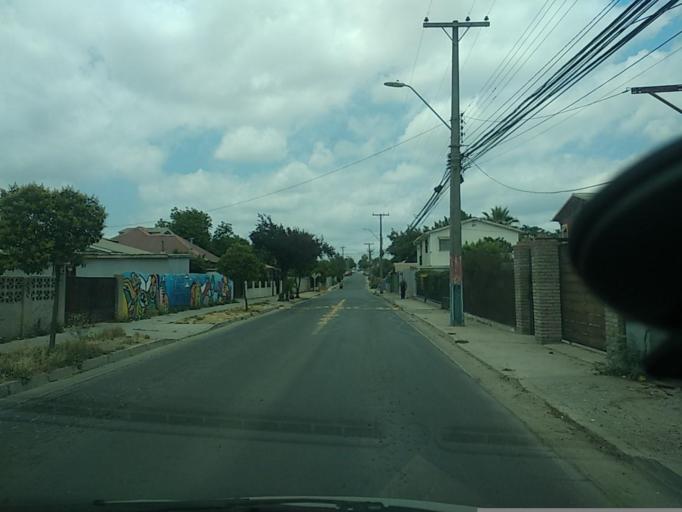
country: CL
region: Valparaiso
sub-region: Provincia de Marga Marga
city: Villa Alemana
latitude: -33.0406
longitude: -71.4076
